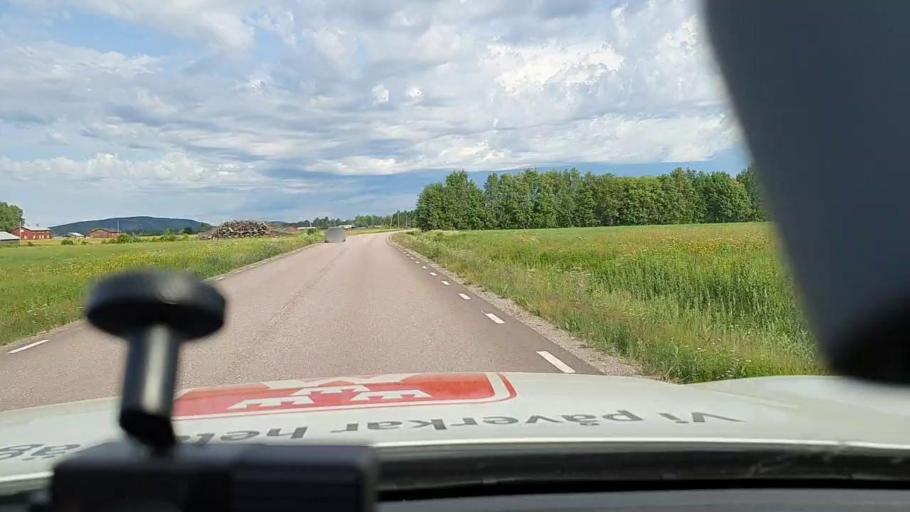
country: SE
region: Norrbotten
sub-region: Bodens Kommun
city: Saevast
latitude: 65.6986
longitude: 21.7741
